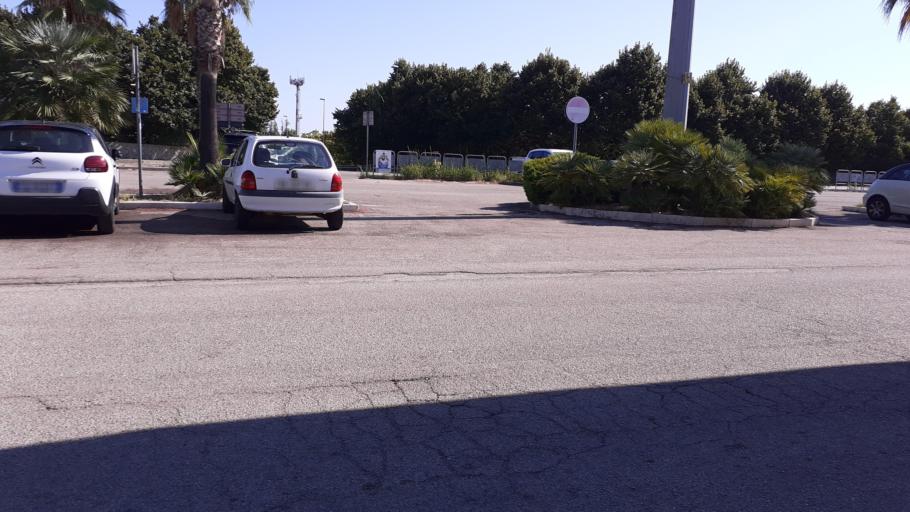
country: IT
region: Abruzzo
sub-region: Provincia di Chieti
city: Marina di Vasto
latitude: 42.0802
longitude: 14.7398
